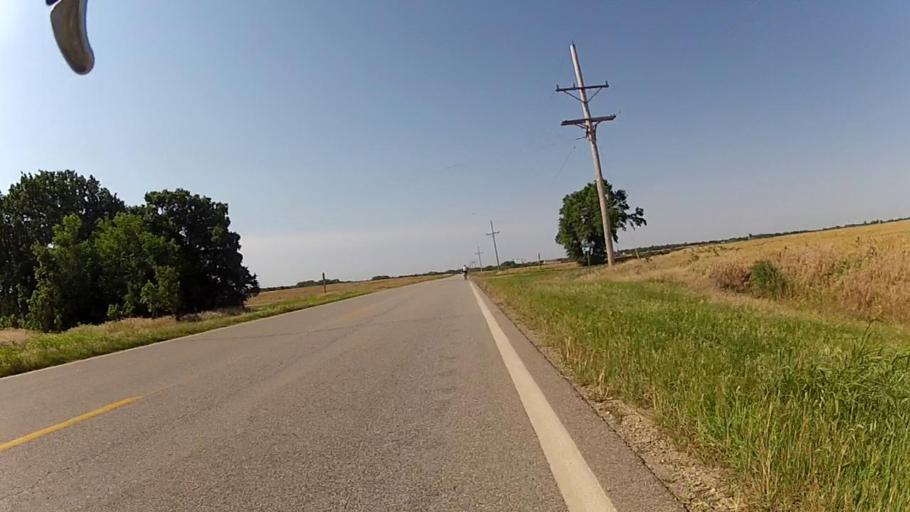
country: US
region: Kansas
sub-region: Sumner County
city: Caldwell
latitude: 37.0555
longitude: -97.6008
